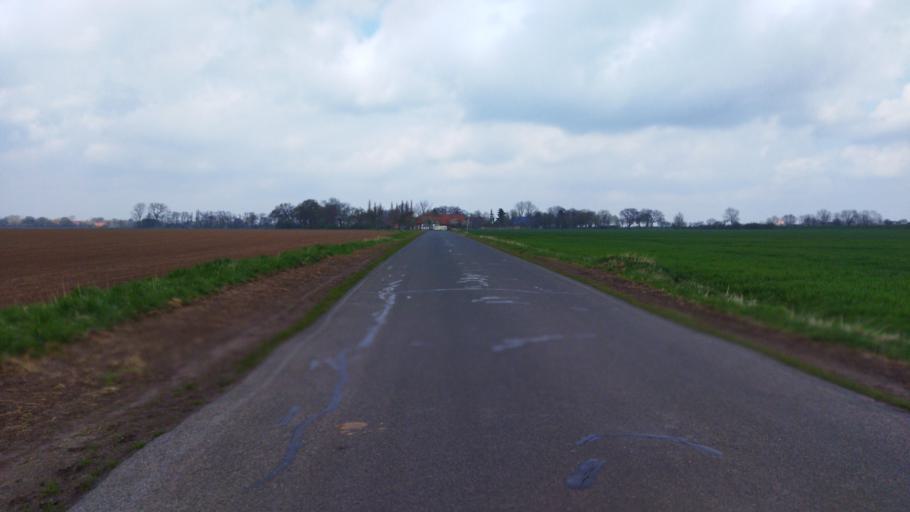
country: DE
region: Lower Saxony
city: Hilgermissen
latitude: 52.8341
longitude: 9.1895
